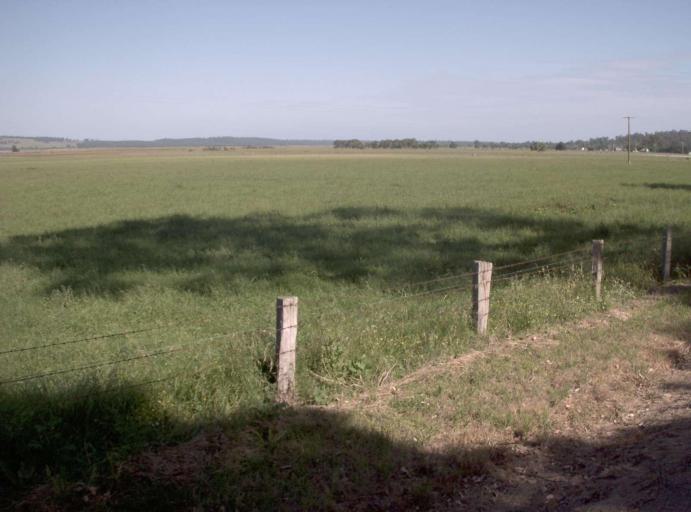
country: AU
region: Victoria
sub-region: East Gippsland
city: Lakes Entrance
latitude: -37.7315
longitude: 148.5046
